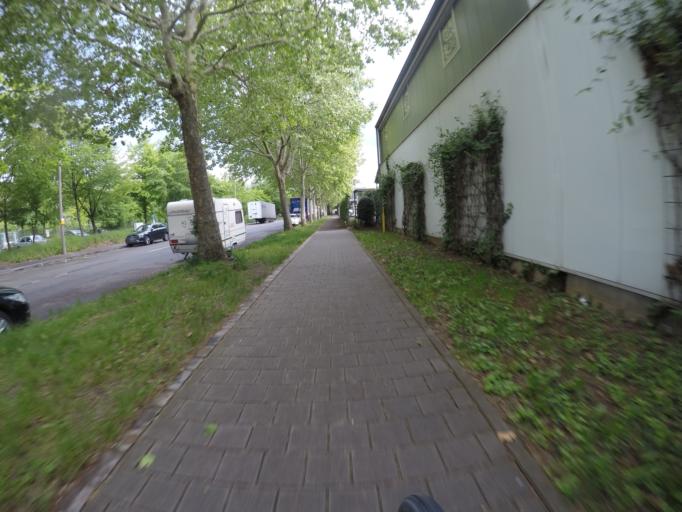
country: DE
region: Baden-Wuerttemberg
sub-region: Regierungsbezirk Stuttgart
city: Ostfildern
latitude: 48.7592
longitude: 9.2674
